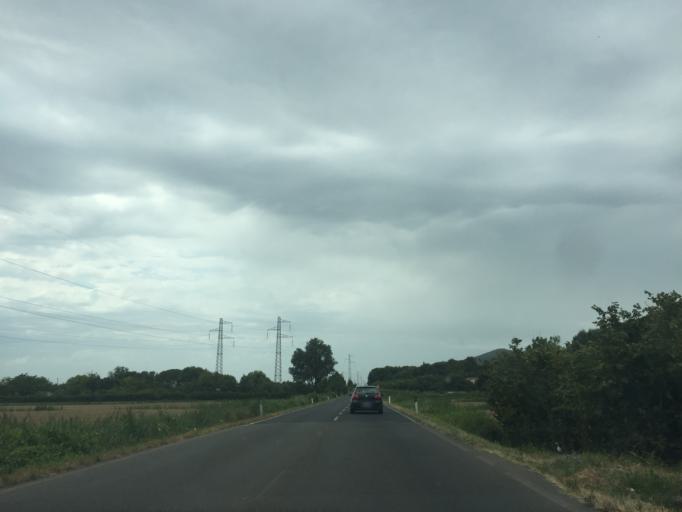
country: IT
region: Tuscany
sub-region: Province of Pisa
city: Gabella
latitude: 43.7298
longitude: 10.4839
